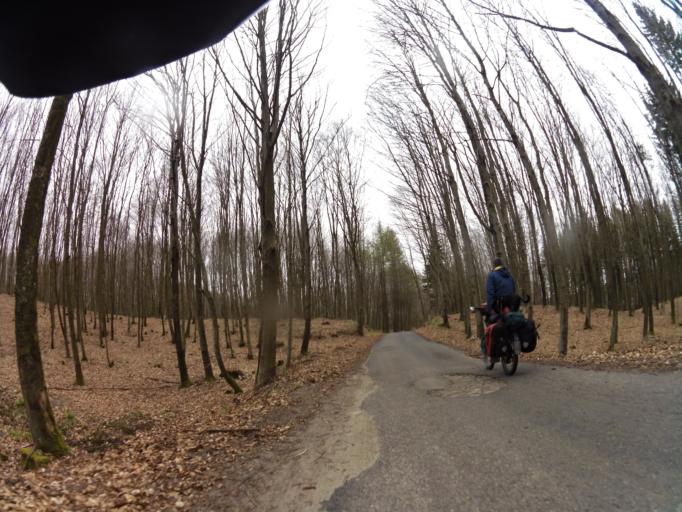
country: PL
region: West Pomeranian Voivodeship
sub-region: Powiat koszalinski
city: Bobolice
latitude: 53.9566
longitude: 16.6620
